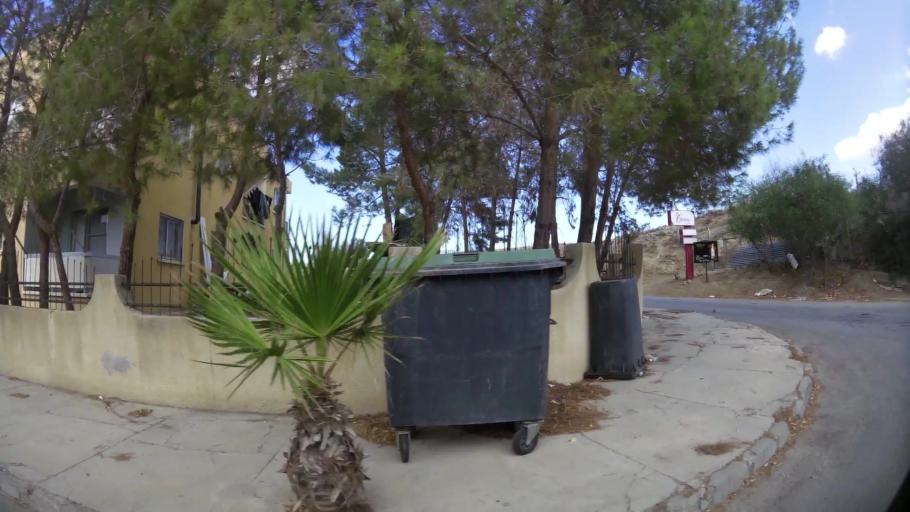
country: CY
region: Lefkosia
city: Nicosia
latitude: 35.2254
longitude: 33.3053
